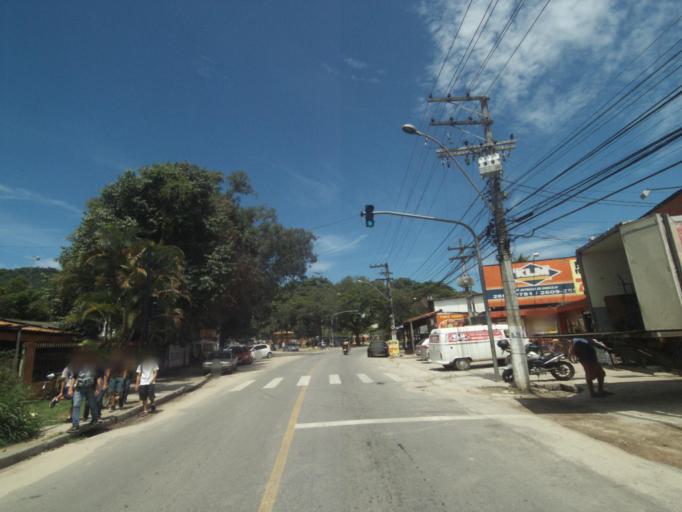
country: BR
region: Rio de Janeiro
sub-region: Niteroi
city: Niteroi
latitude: -22.9342
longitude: -43.0088
